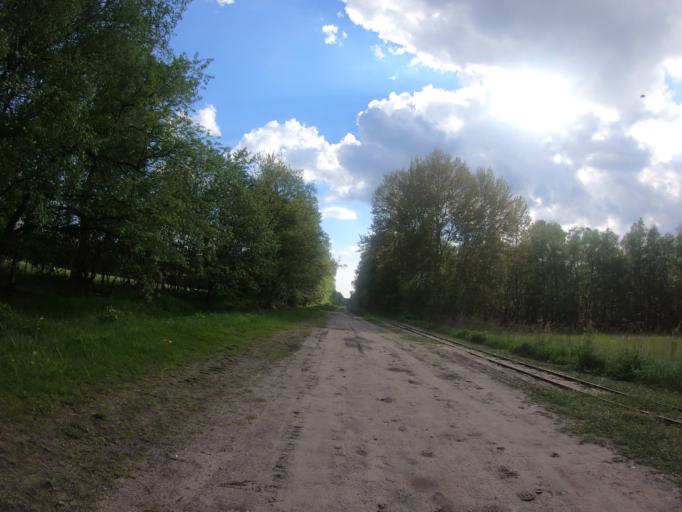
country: DE
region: Lower Saxony
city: Sassenburg
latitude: 52.5179
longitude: 10.6250
